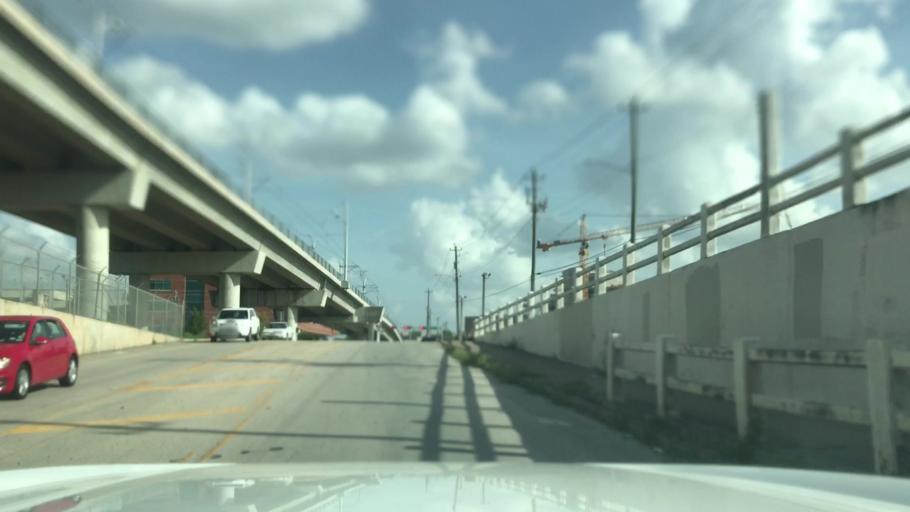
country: US
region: Texas
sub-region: Harris County
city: Houston
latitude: 29.7710
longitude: -95.3592
